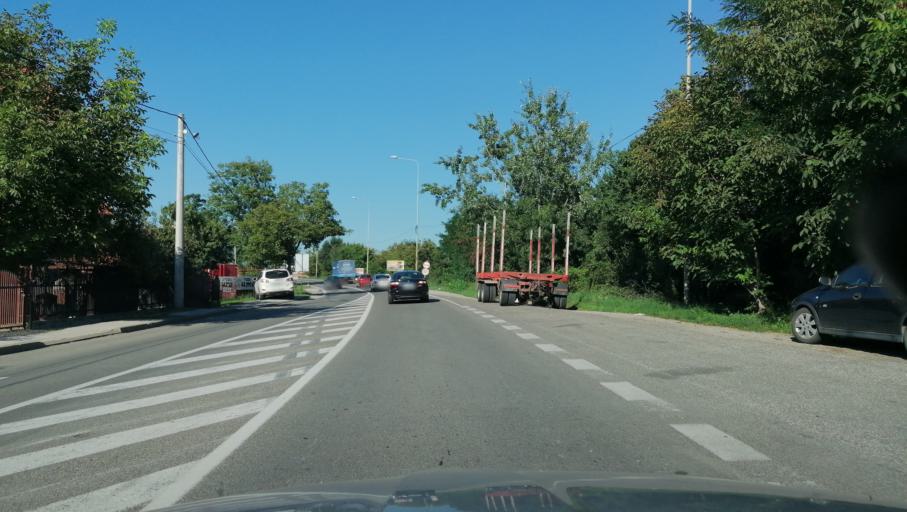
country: RS
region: Central Serbia
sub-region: Raski Okrug
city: Kraljevo
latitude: 43.7233
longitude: 20.6467
